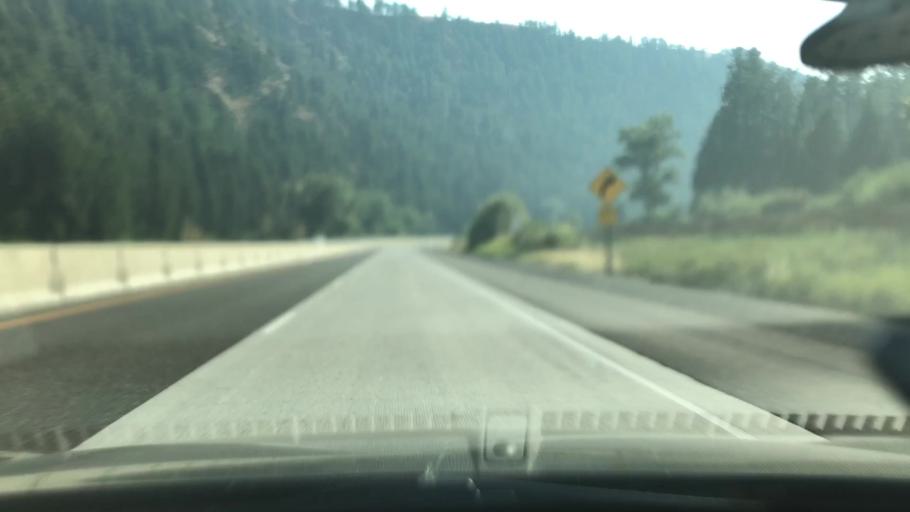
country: US
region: Oregon
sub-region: Union County
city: La Grande
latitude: 45.3502
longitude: -118.1989
